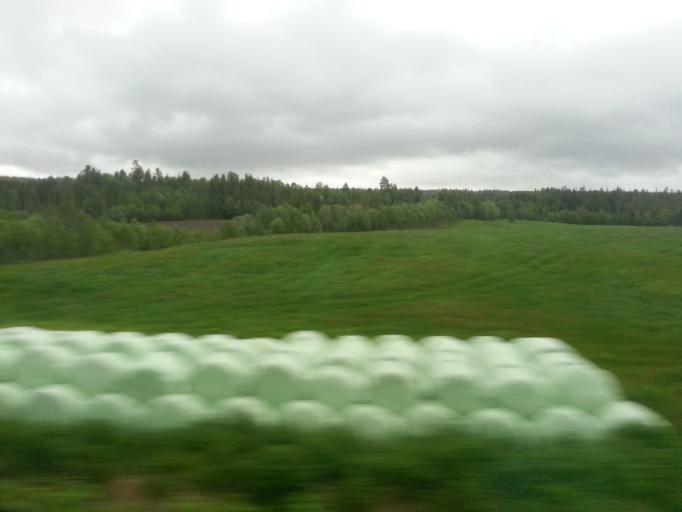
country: NO
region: Sor-Trondelag
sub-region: Rennebu
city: Berkak
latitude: 62.8794
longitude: 10.0959
